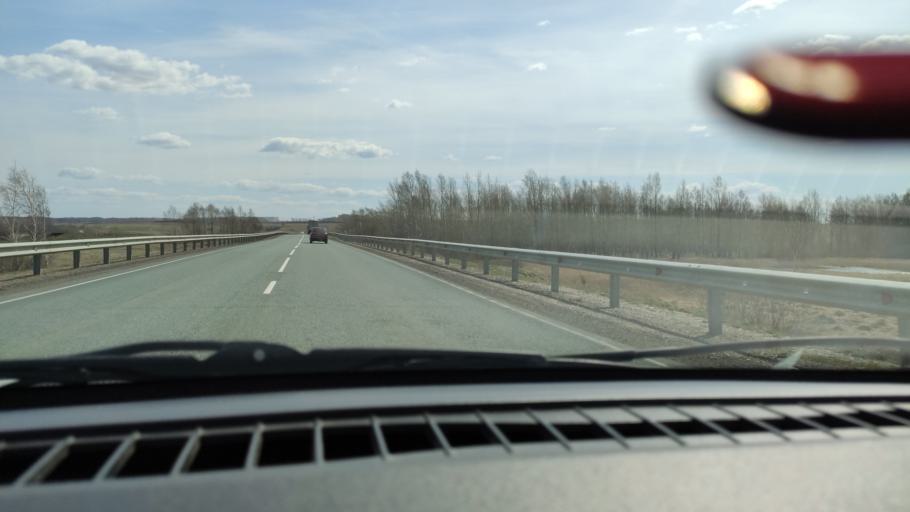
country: RU
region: Bashkortostan
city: Kushnarenkovo
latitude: 55.1497
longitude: 55.1481
